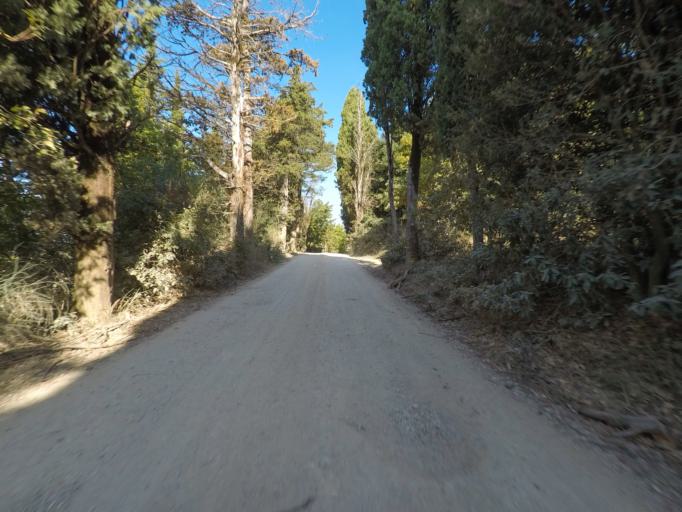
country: IT
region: Tuscany
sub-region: Provincia di Siena
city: Castellina in Chianti
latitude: 43.4332
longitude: 11.3330
